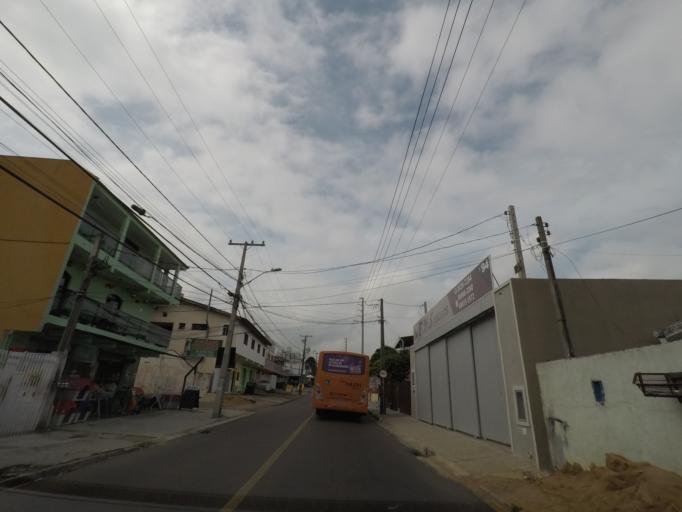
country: BR
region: Parana
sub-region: Curitiba
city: Curitiba
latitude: -25.4943
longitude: -49.3018
